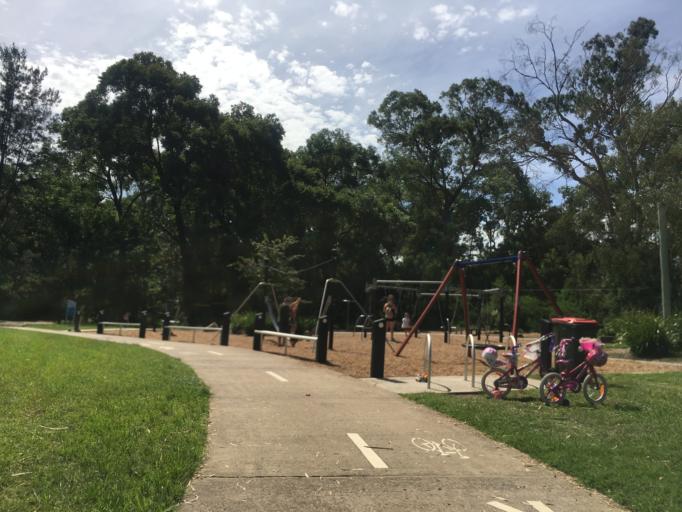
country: AU
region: New South Wales
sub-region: Camden
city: Elderslie
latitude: -34.0607
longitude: 150.7009
